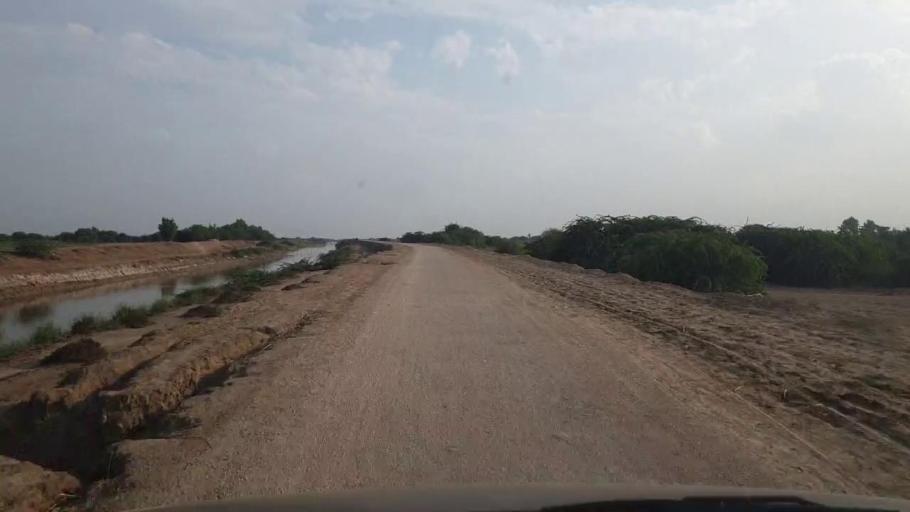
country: PK
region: Sindh
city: Badin
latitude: 24.5483
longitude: 68.6713
